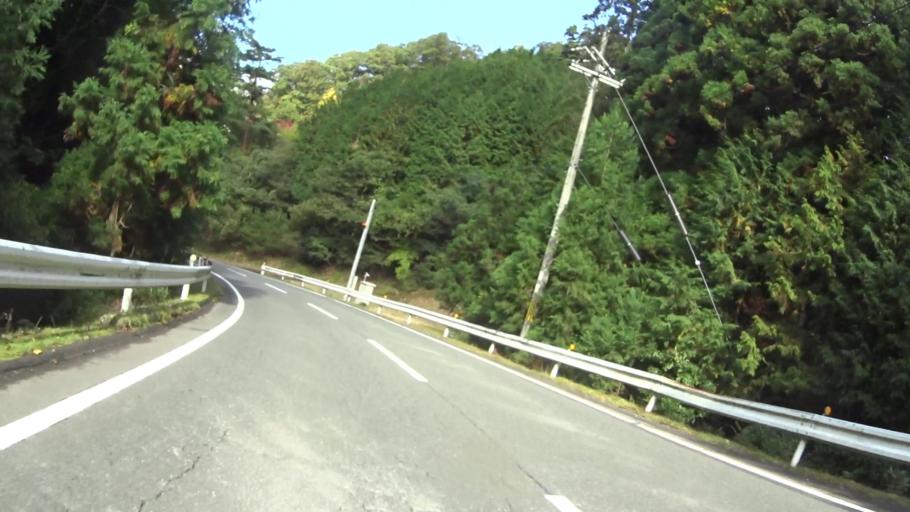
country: JP
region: Hyogo
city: Toyooka
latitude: 35.5355
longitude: 134.9790
